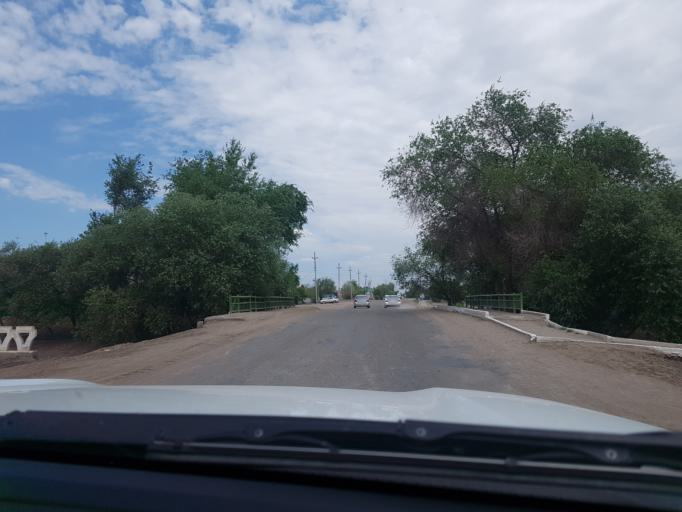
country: TM
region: Dasoguz
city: Koeneuergench
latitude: 42.3120
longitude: 59.1379
